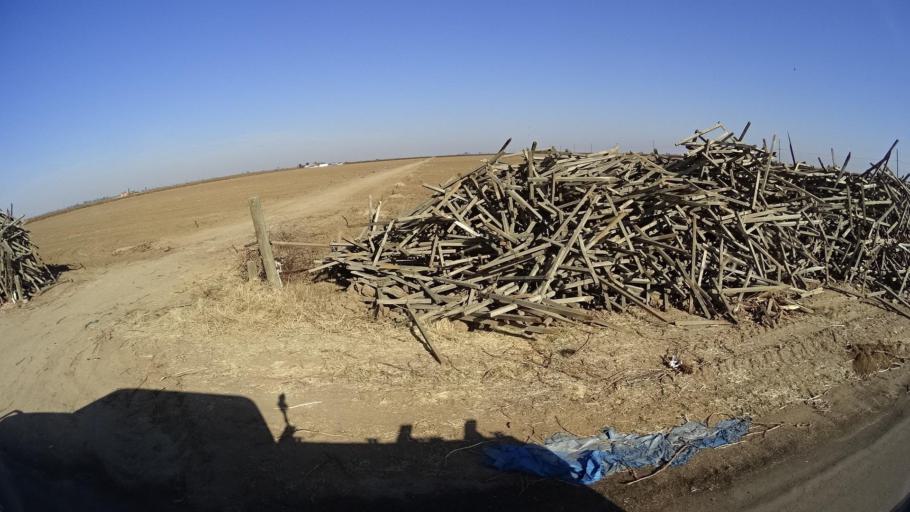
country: US
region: California
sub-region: Kern County
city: Delano
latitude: 35.7324
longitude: -119.2072
